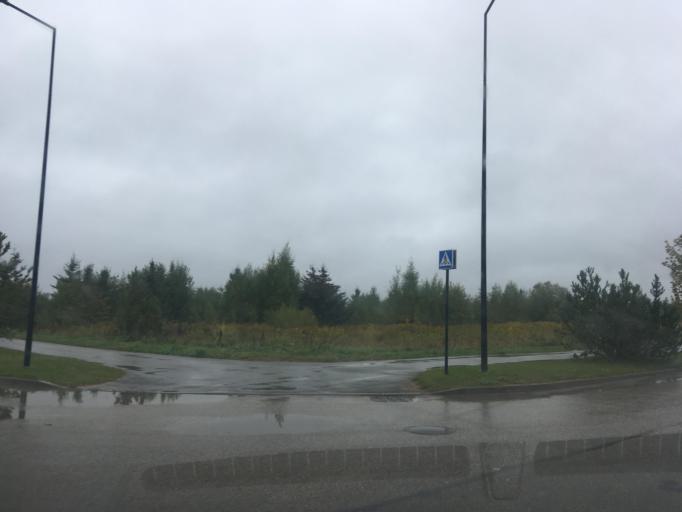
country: EE
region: Tartu
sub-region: UElenurme vald
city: Ulenurme
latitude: 58.3396
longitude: 26.7889
